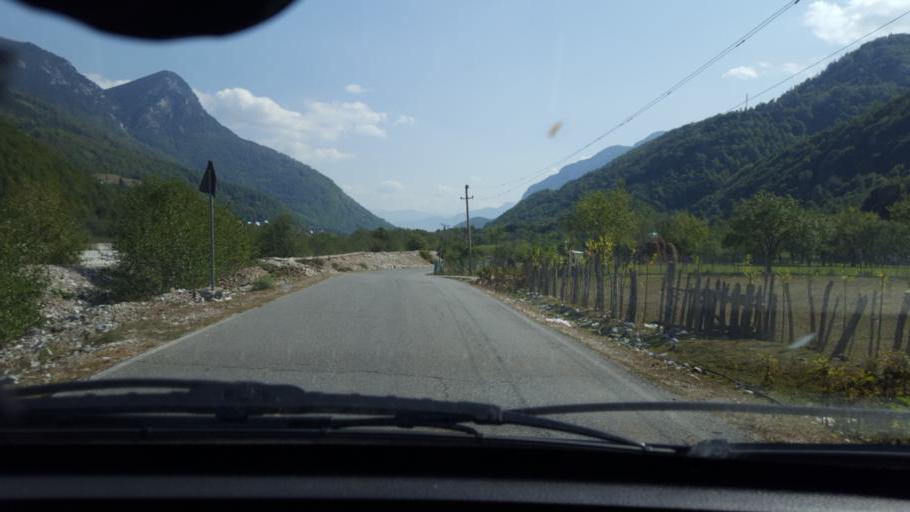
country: ME
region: Andrijevica
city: Andrijevica
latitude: 42.5893
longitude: 19.6988
